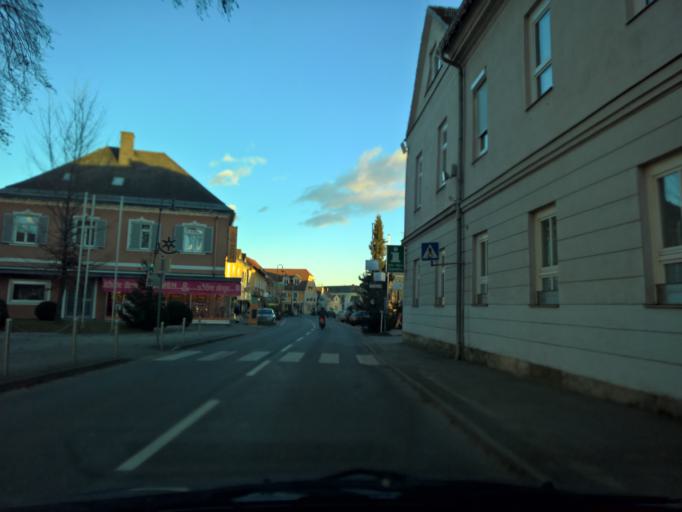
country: AT
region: Styria
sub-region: Politischer Bezirk Leibnitz
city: Gamlitz
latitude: 46.7206
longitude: 15.5541
